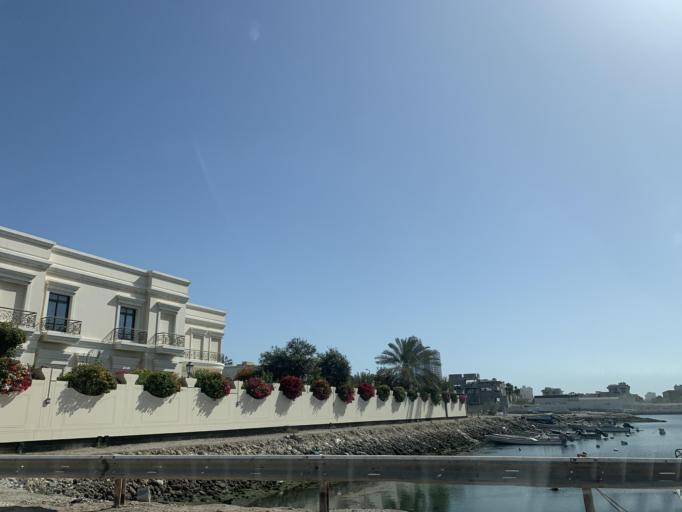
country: BH
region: Manama
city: Manama
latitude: 26.2015
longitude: 50.5706
